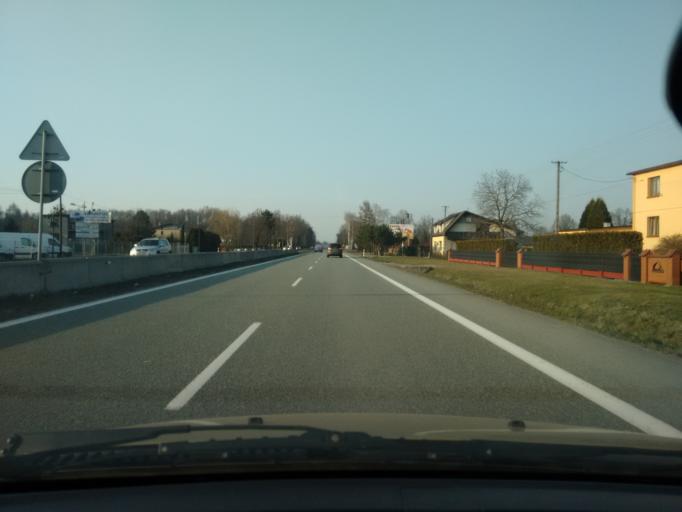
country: PL
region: Silesian Voivodeship
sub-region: Powiat cieszynski
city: Zbytkow
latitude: 49.9067
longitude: 18.7360
